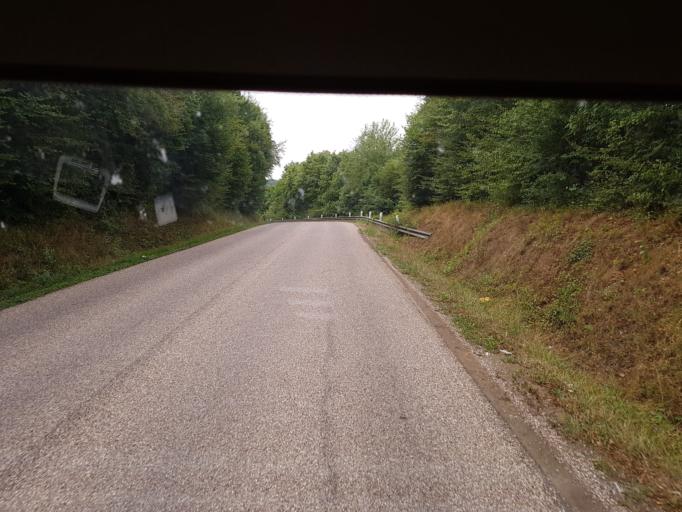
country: FR
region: Lorraine
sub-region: Departement de Meurthe-et-Moselle
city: Joeuf
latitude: 49.2423
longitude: 6.0314
